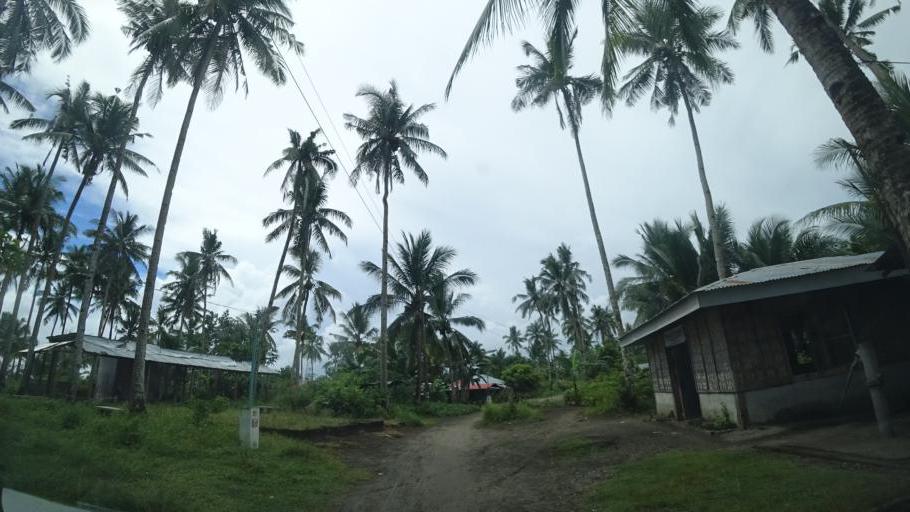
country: PH
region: Eastern Visayas
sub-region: Province of Leyte
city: Liberty
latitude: 10.8540
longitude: 125.0035
